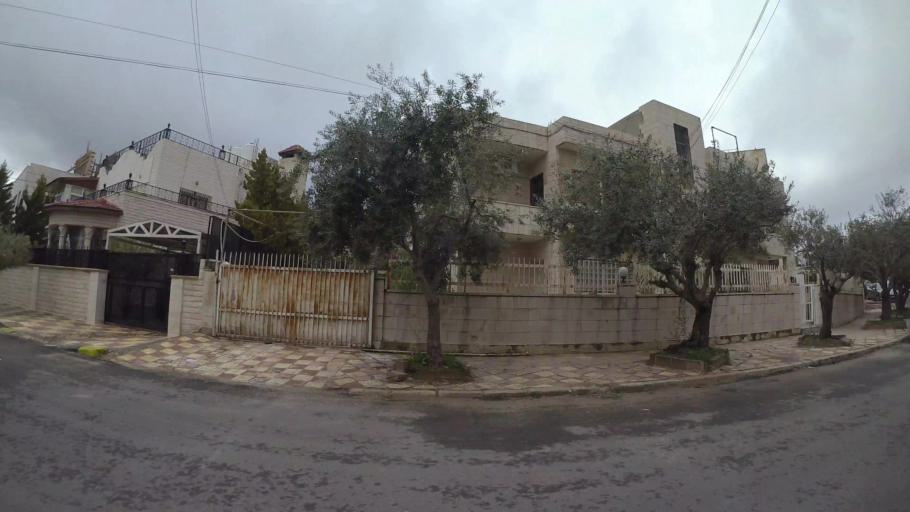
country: JO
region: Amman
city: Amman
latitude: 31.9410
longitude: 35.9052
